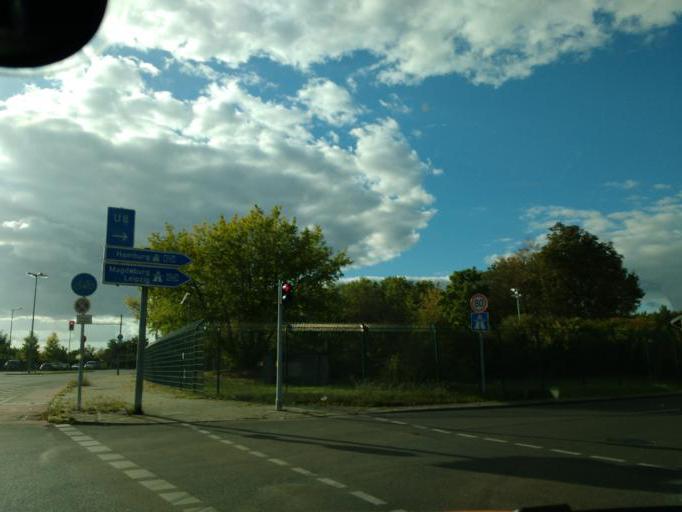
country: DE
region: Berlin
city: Britz
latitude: 52.4517
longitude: 13.4164
